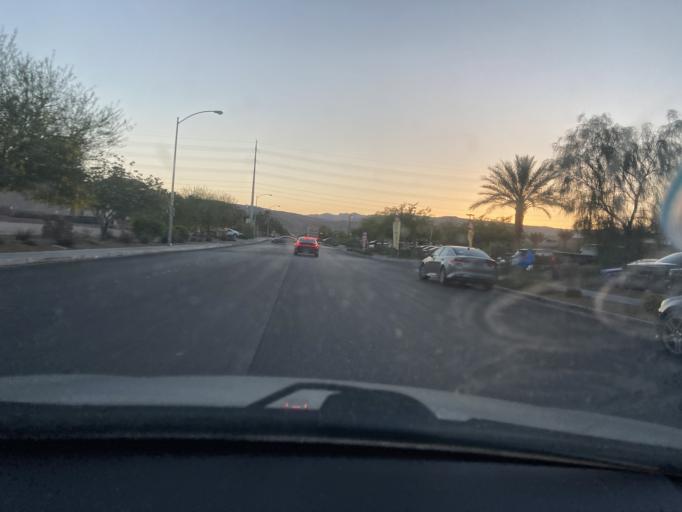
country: US
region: Nevada
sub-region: Clark County
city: Enterprise
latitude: 36.0593
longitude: -115.2771
